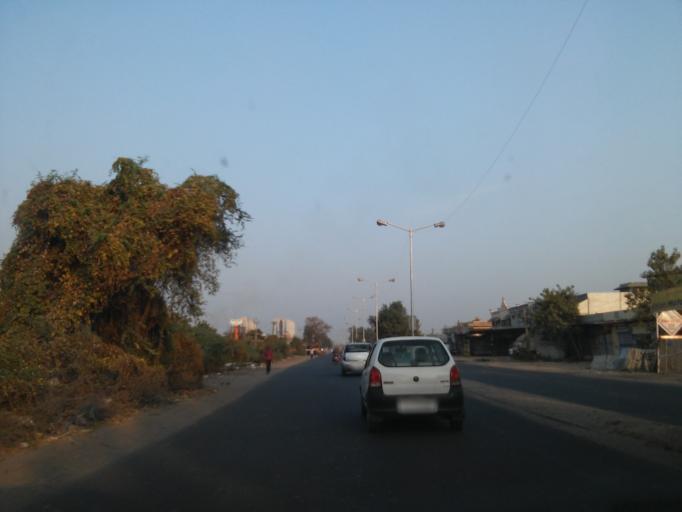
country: IN
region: Gujarat
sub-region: Ahmadabad
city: Sarkhej
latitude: 22.9875
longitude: 72.4858
